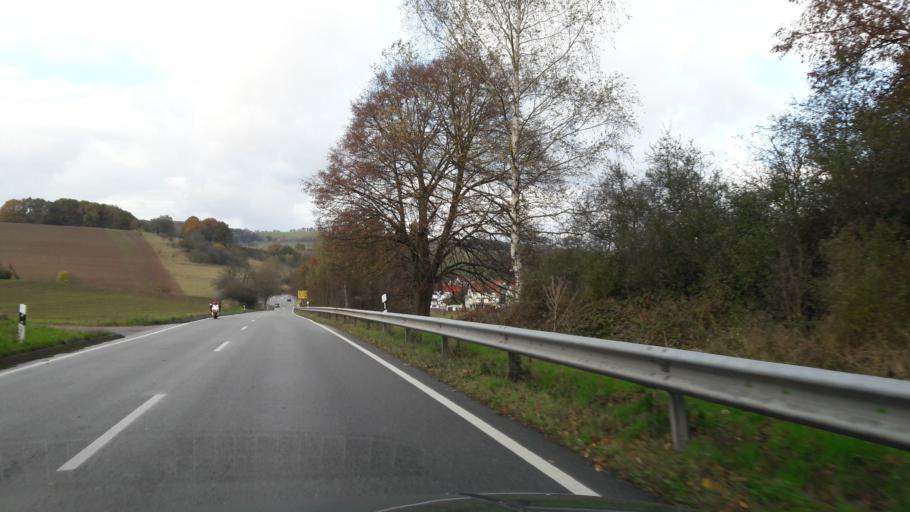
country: DE
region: Rheinland-Pfalz
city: Krottelbach
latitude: 49.4672
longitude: 7.3461
